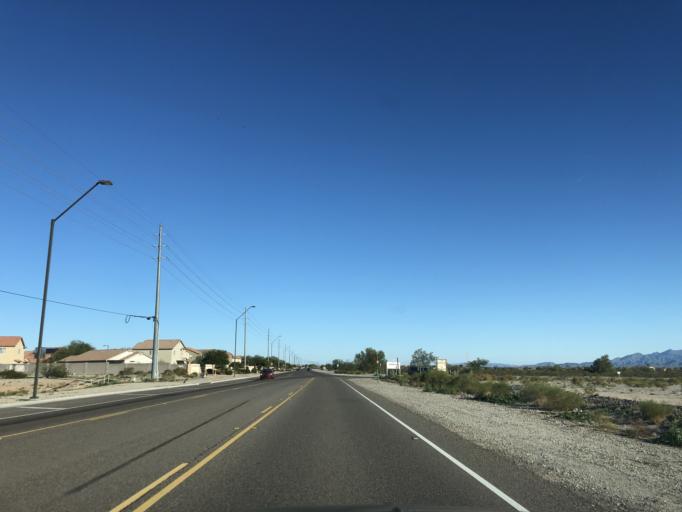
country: US
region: Arizona
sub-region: Maricopa County
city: Buckeye
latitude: 33.4354
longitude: -112.5748
